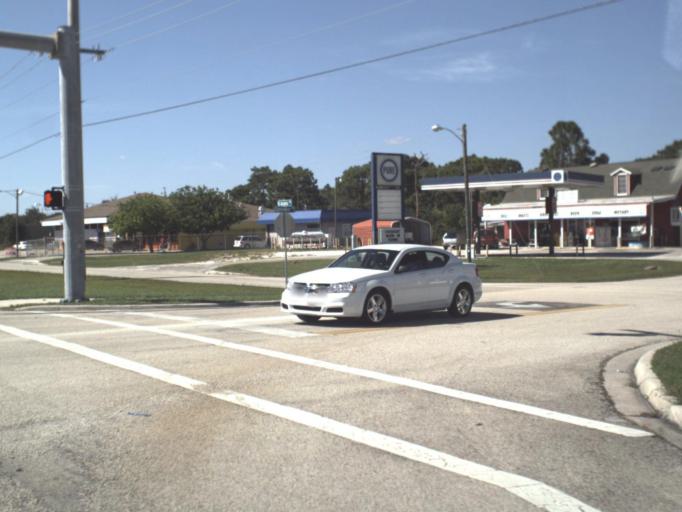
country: US
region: Florida
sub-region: Charlotte County
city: Grove City
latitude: 26.9335
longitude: -82.2883
